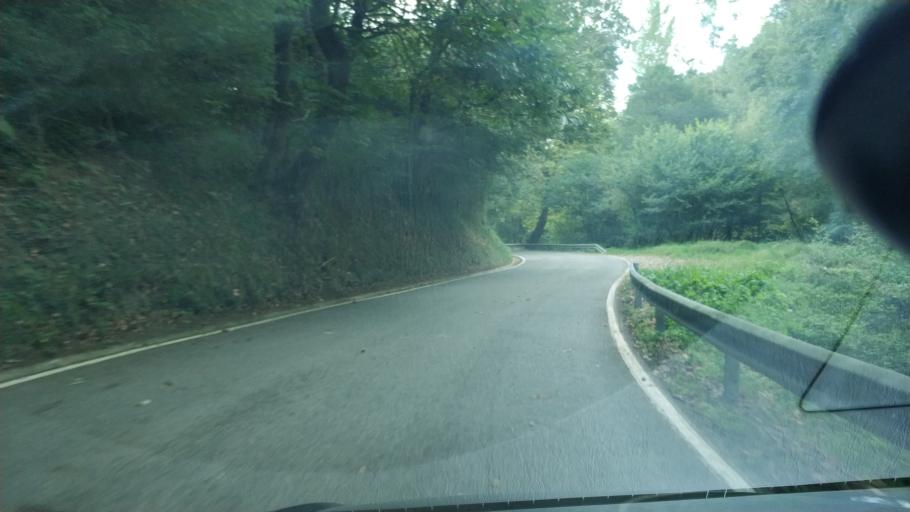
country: ES
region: Cantabria
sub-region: Provincia de Cantabria
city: Santa Maria de Cayon
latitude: 43.2853
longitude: -3.8161
